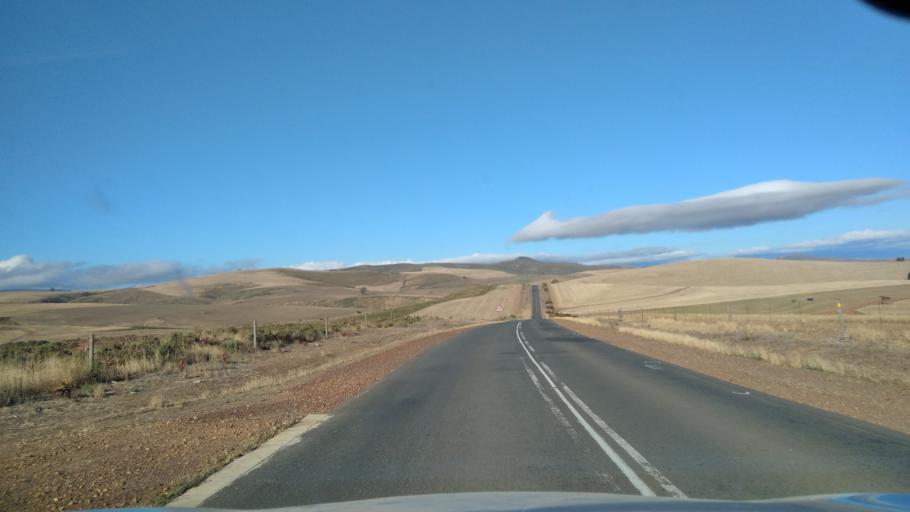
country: ZA
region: Western Cape
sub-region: Overberg District Municipality
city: Caledon
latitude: -34.1736
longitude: 19.2825
